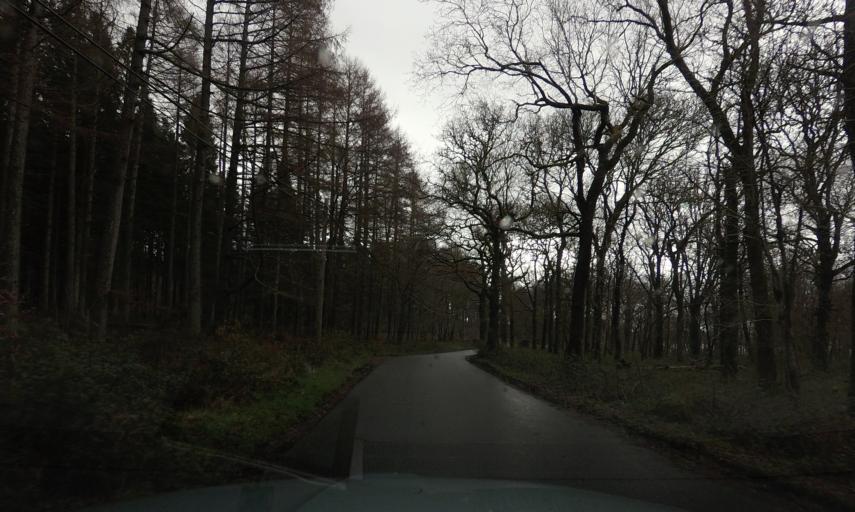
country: GB
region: Scotland
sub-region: West Dunbartonshire
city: Balloch
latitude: 56.1290
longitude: -4.6078
